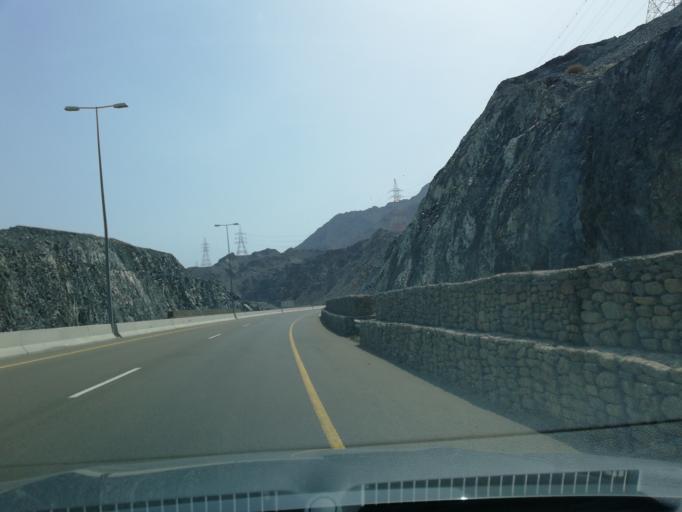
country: OM
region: Al Batinah
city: Al Liwa'
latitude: 24.2438
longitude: 56.3523
